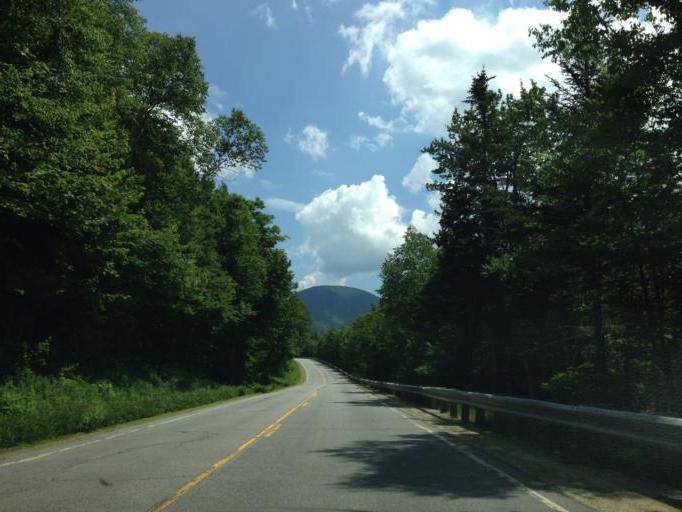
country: US
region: New Hampshire
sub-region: Grafton County
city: Woodstock
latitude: 44.0390
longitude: -71.5222
